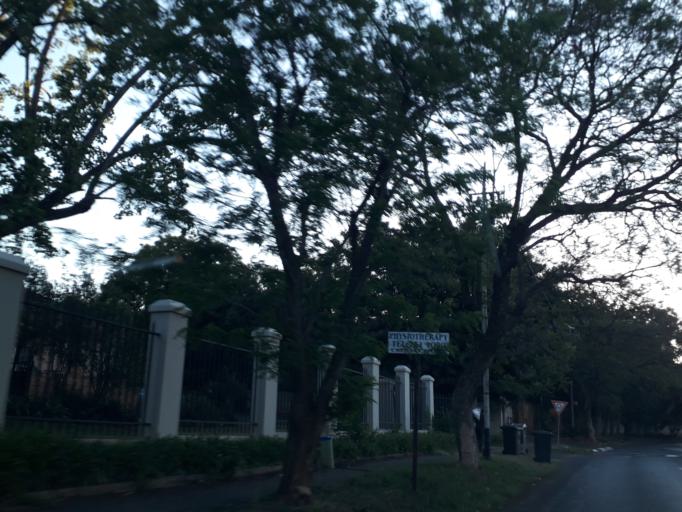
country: ZA
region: Gauteng
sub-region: City of Johannesburg Metropolitan Municipality
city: Roodepoort
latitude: -26.1360
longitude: 27.9667
